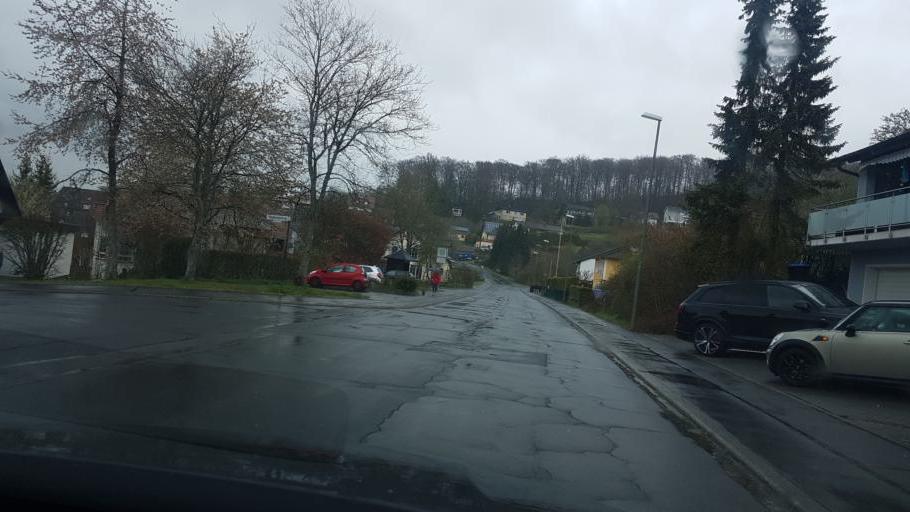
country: DE
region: Rheinland-Pfalz
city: Pelm
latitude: 50.2320
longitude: 6.6929
